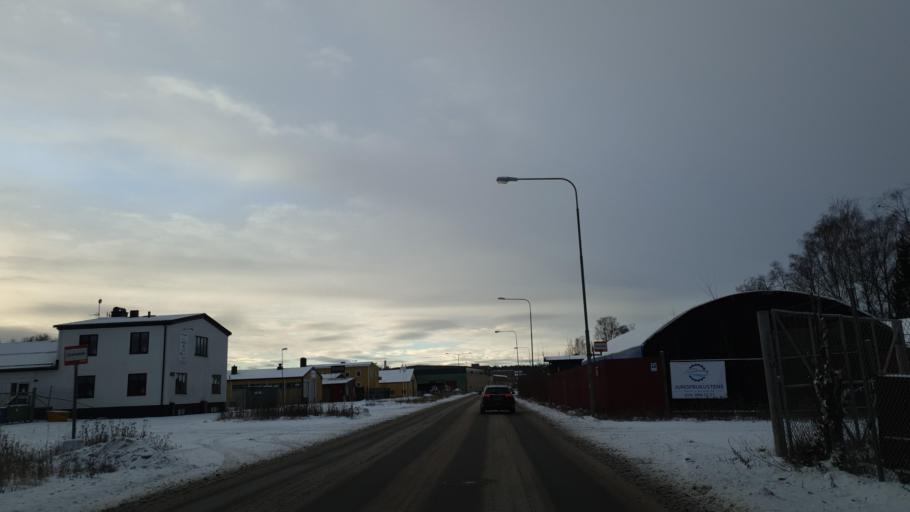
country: SE
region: Gaevleborg
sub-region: Soderhamns Kommun
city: Soderhamn
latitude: 61.3109
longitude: 17.0751
